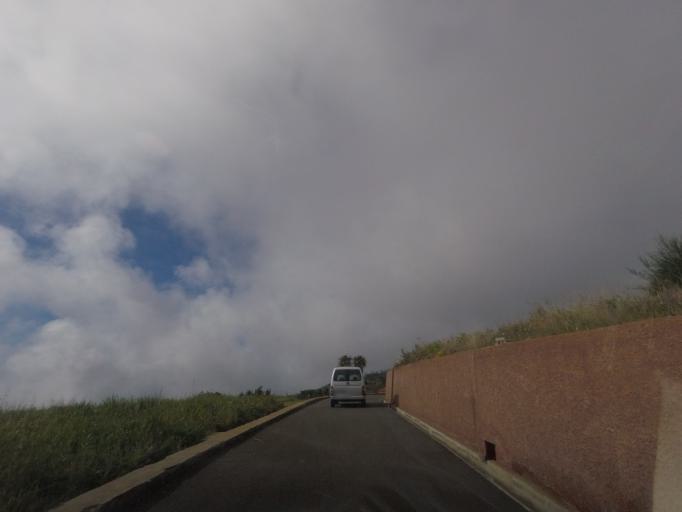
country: PT
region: Madeira
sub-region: Calheta
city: Faja da Ovelha
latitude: 32.7662
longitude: -17.2215
